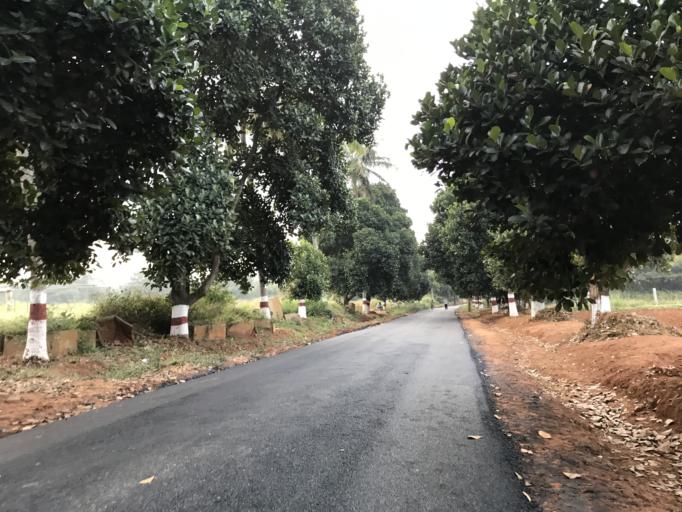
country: IN
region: Karnataka
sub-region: Bangalore Urban
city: Yelahanka
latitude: 13.0807
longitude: 77.5699
